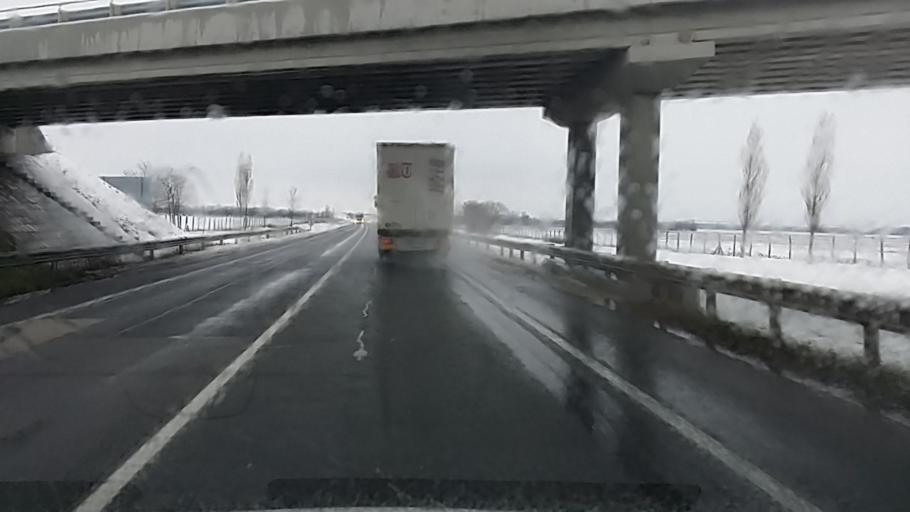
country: HU
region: Gyor-Moson-Sopron
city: Rajka
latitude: 47.9141
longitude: 17.1804
